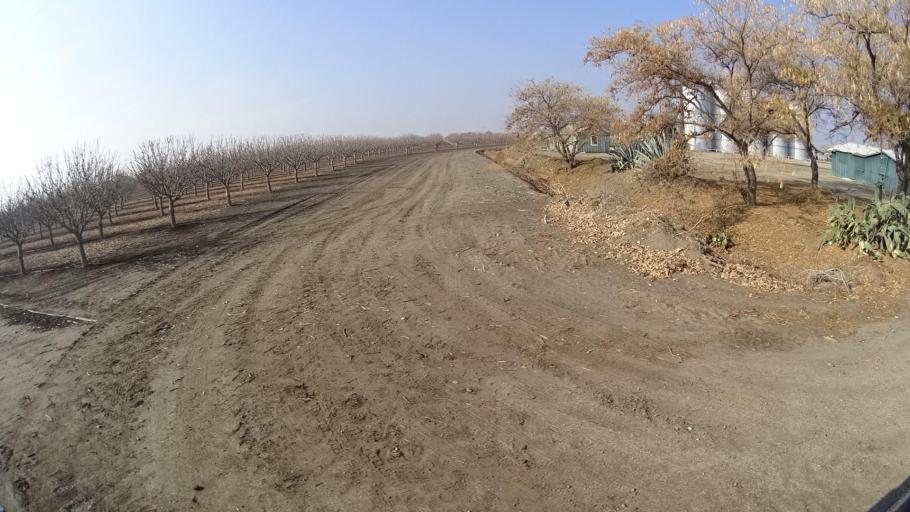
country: US
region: California
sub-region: Kern County
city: Buttonwillow
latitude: 35.3904
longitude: -119.4477
